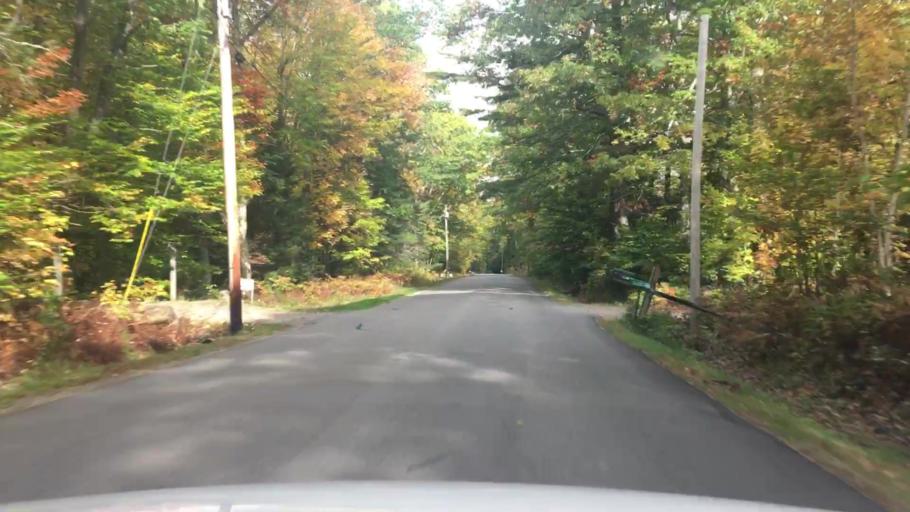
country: US
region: Maine
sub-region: Knox County
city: Camden
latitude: 44.2230
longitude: -69.1026
